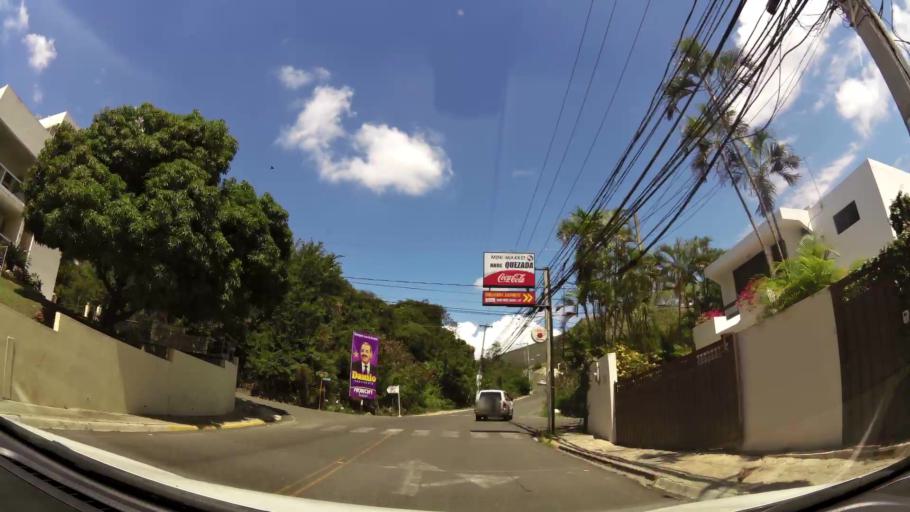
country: DO
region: Santiago
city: Santiago de los Caballeros
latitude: 19.4643
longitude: -70.6806
